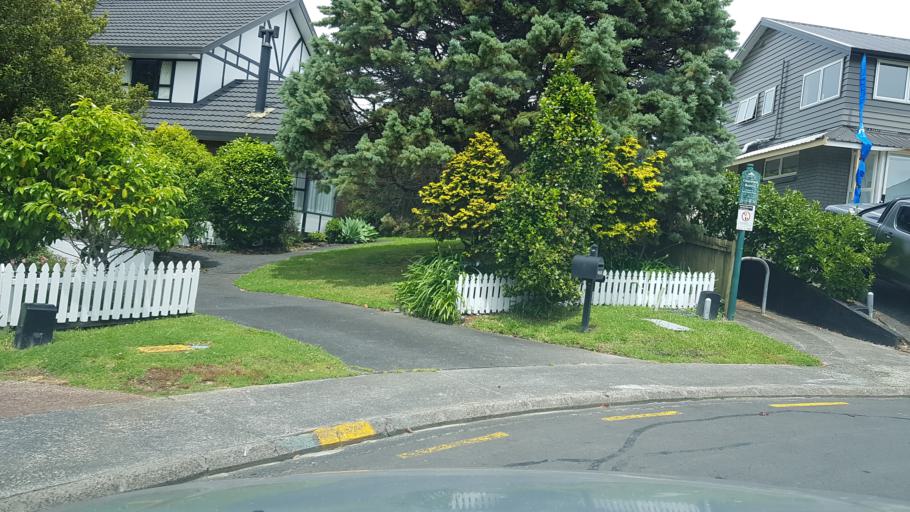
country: NZ
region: Auckland
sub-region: Auckland
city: North Shore
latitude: -36.8201
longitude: 174.7154
